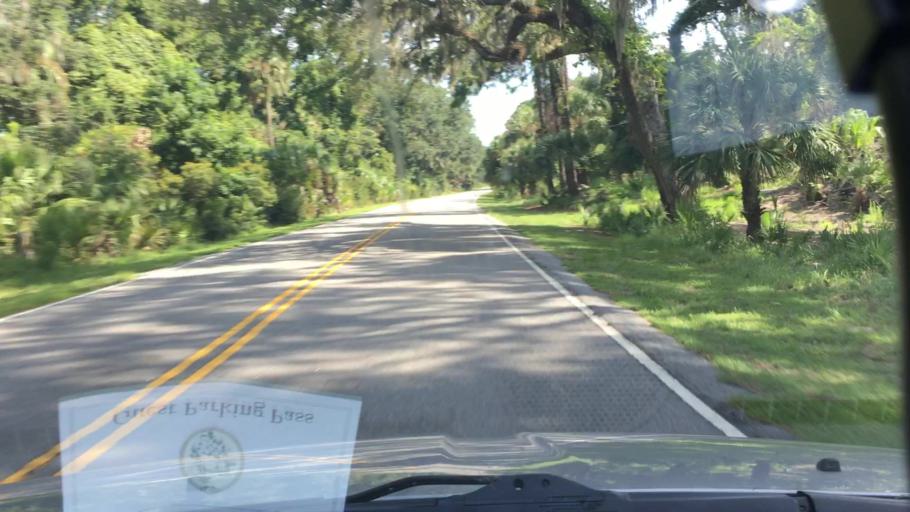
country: US
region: South Carolina
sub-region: Beaufort County
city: Beaufort
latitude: 32.3785
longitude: -80.4450
